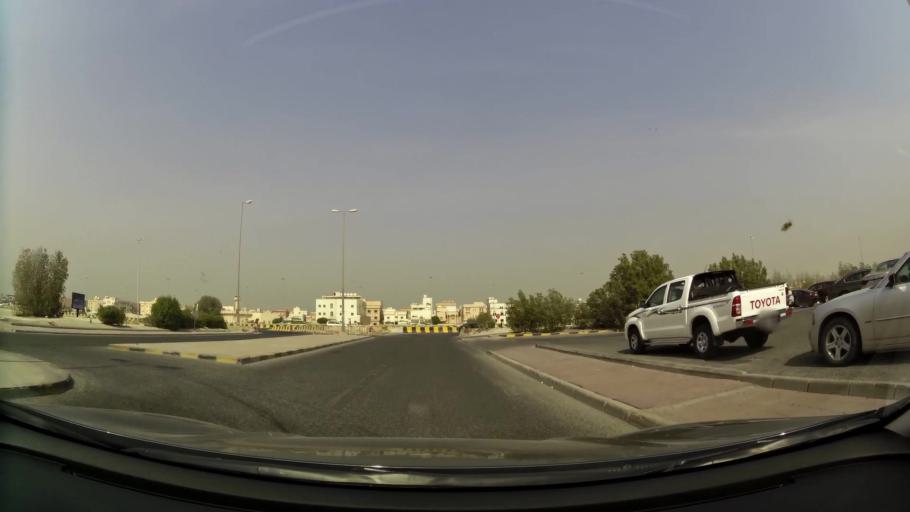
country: KW
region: Al Asimah
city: Ar Rabiyah
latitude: 29.3087
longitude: 47.8737
